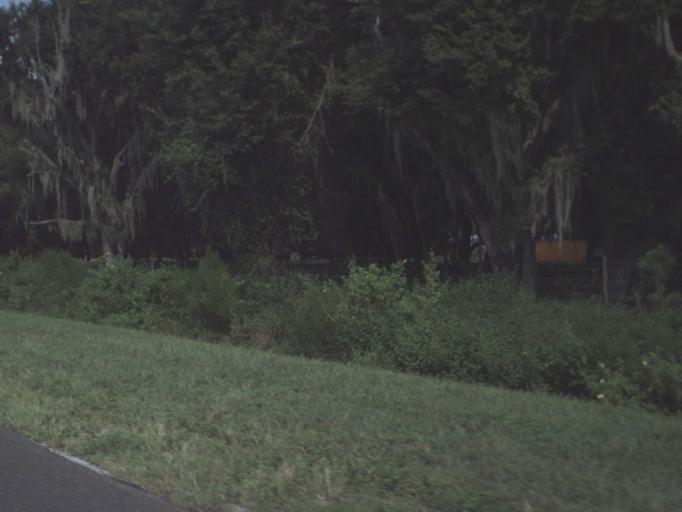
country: US
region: Florida
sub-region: Polk County
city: Crooked Lake Park
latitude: 27.8141
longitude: -81.5970
